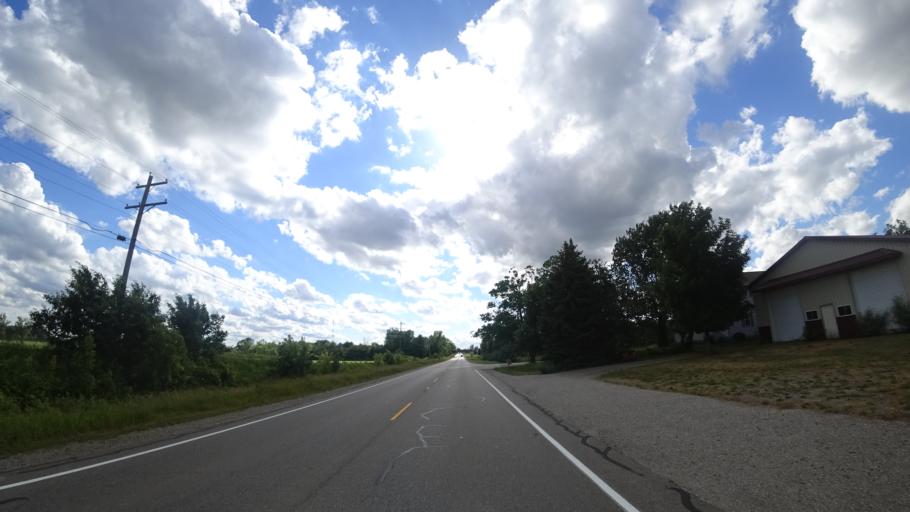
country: US
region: Michigan
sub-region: Ionia County
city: Portland
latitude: 42.8716
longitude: -84.9447
